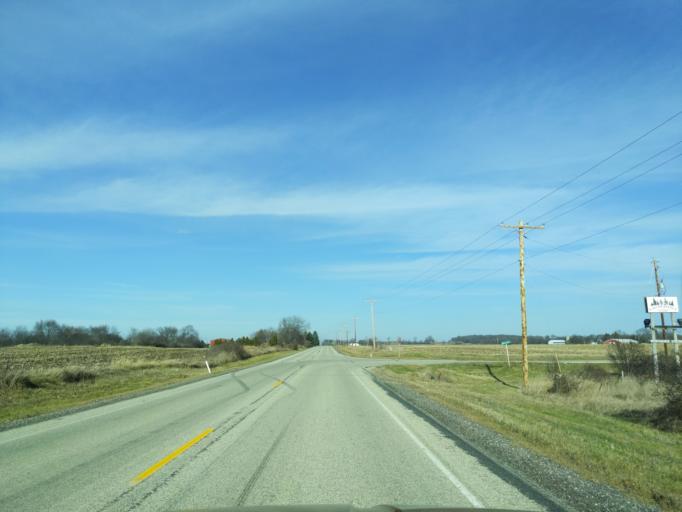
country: US
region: Wisconsin
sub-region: Jefferson County
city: Palmyra
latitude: 42.7734
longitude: -88.6030
